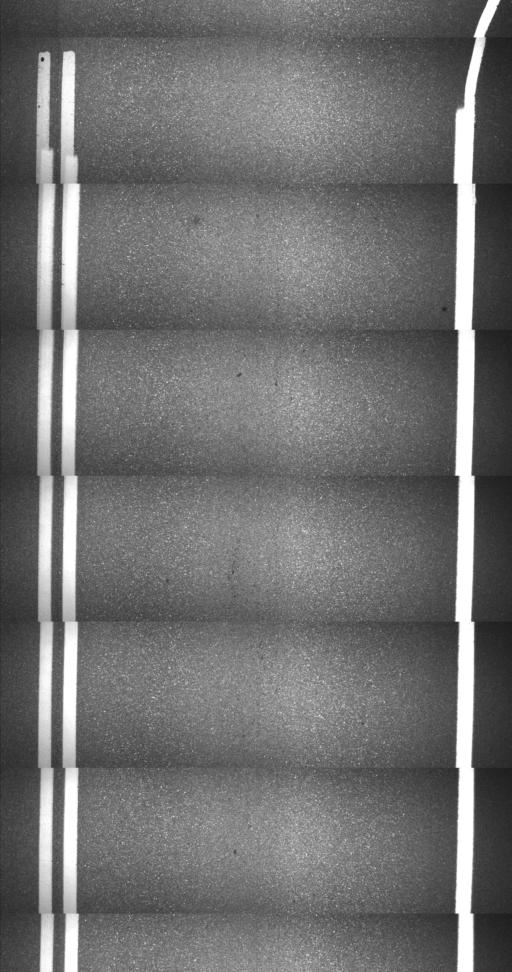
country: US
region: Vermont
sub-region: Windham County
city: Dover
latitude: 43.0682
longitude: -72.8624
